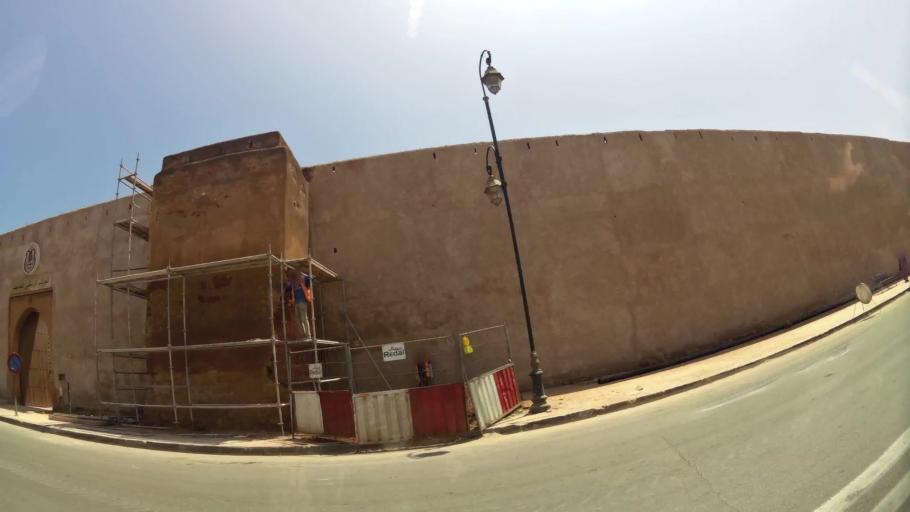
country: MA
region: Rabat-Sale-Zemmour-Zaer
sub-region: Rabat
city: Rabat
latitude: 34.0236
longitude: -6.8410
